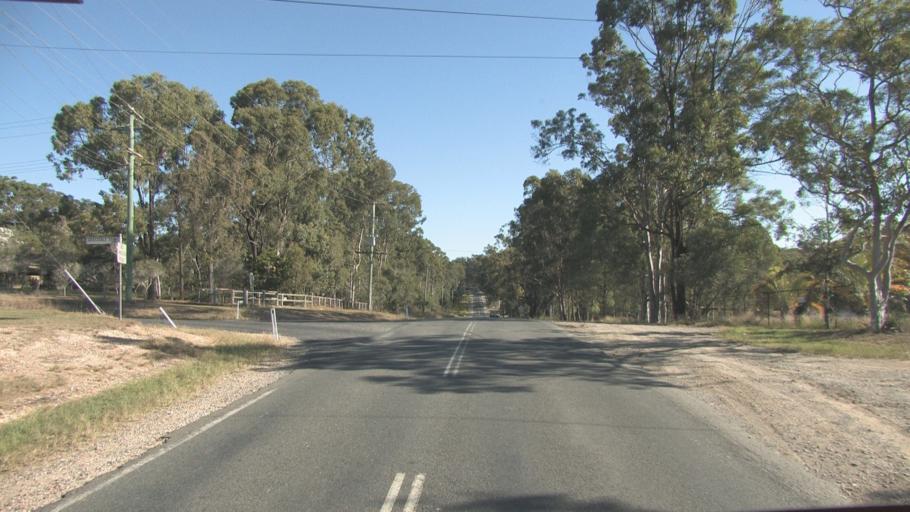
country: AU
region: Queensland
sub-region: Logan
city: Waterford West
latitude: -27.7393
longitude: 153.1476
